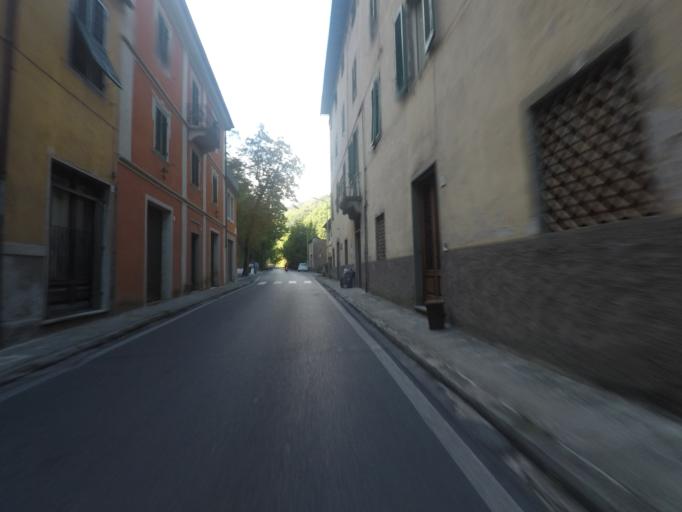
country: IT
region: Tuscany
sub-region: Provincia di Lucca
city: Bagni di Lucca
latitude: 44.0069
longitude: 10.5793
